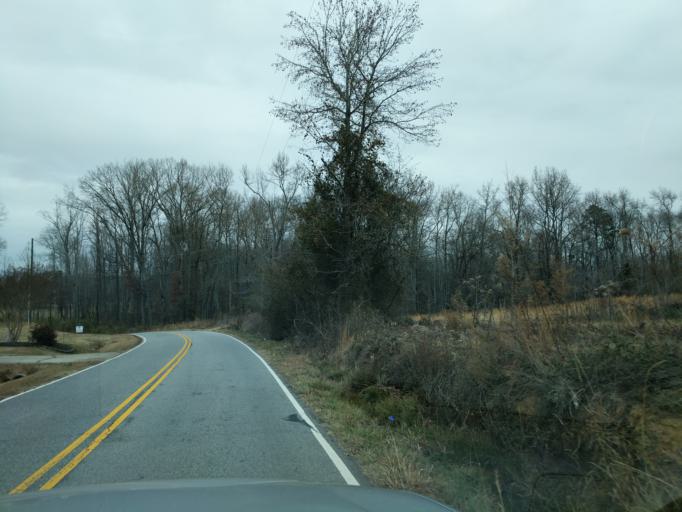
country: US
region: South Carolina
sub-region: Spartanburg County
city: Duncan
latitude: 34.8682
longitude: -82.1271
